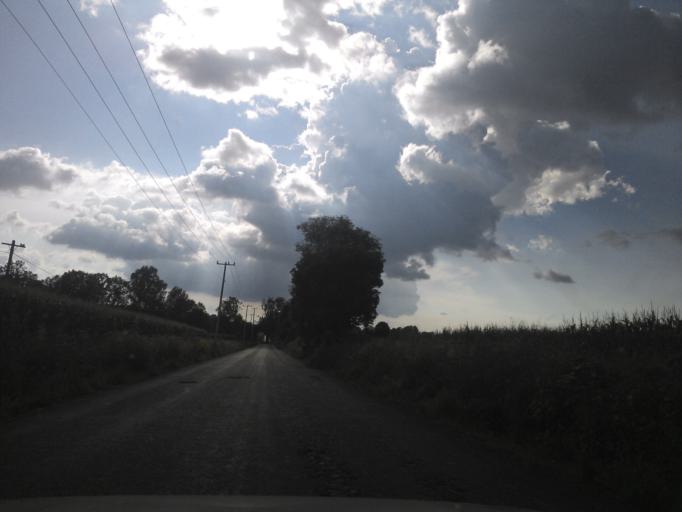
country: MX
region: Jalisco
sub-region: Atotonilco el Alto
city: Ojo de Agua de Moran
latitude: 20.6028
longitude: -102.4771
